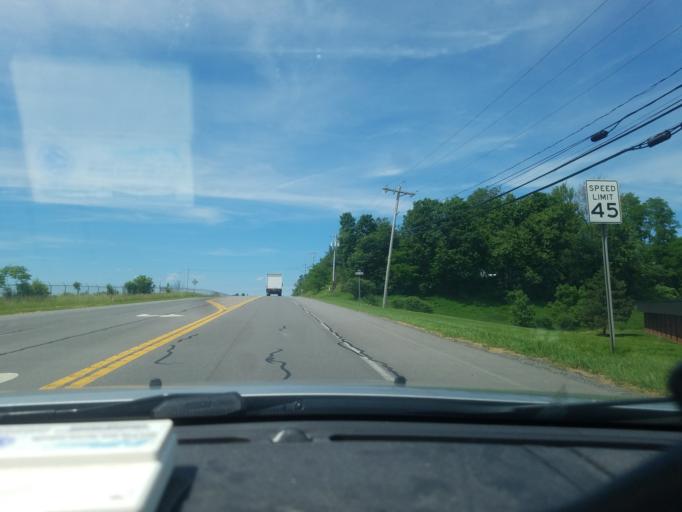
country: US
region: New York
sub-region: Onondaga County
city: East Syracuse
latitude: 43.0869
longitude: -76.0589
